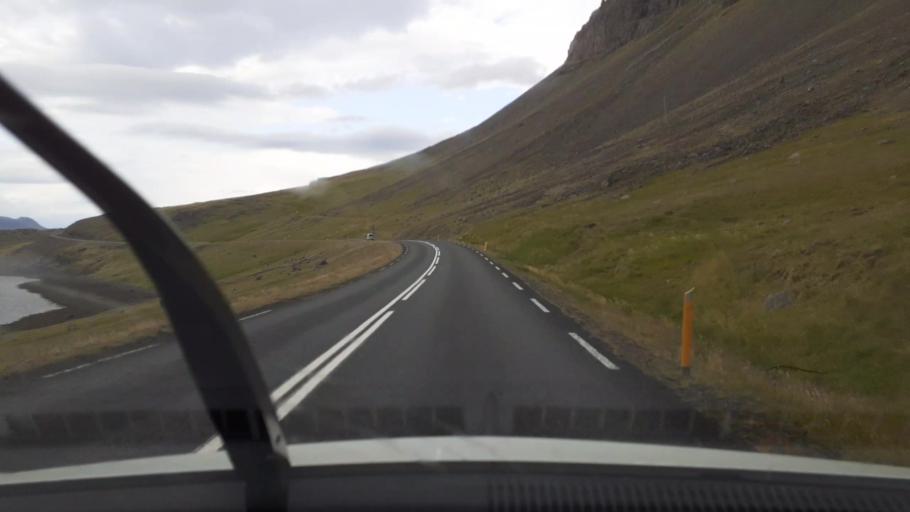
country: IS
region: Capital Region
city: Mosfellsbaer
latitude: 64.3886
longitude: -21.3943
